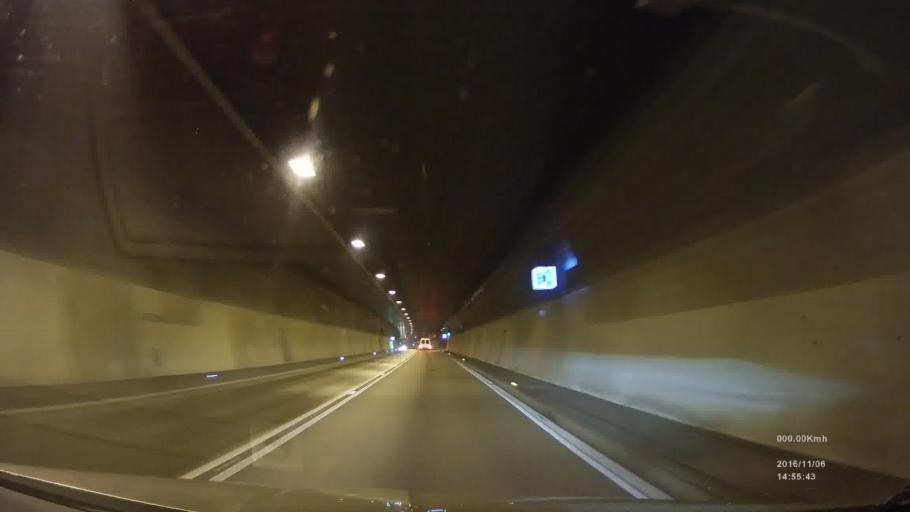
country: SK
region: Kosicky
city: Krompachy
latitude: 48.9987
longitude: 20.8963
